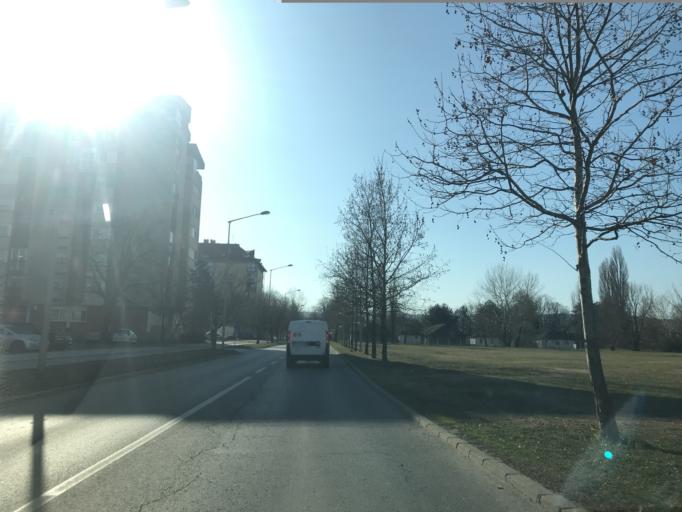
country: RS
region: Autonomna Pokrajina Vojvodina
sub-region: Juznobacki Okrug
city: Novi Sad
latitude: 45.2368
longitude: 19.8266
